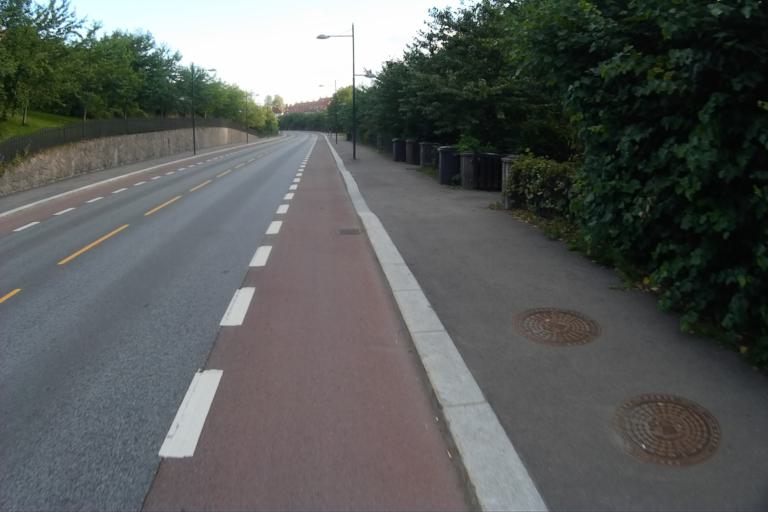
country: NO
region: Oslo
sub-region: Oslo
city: Oslo
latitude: 59.9438
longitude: 10.7308
